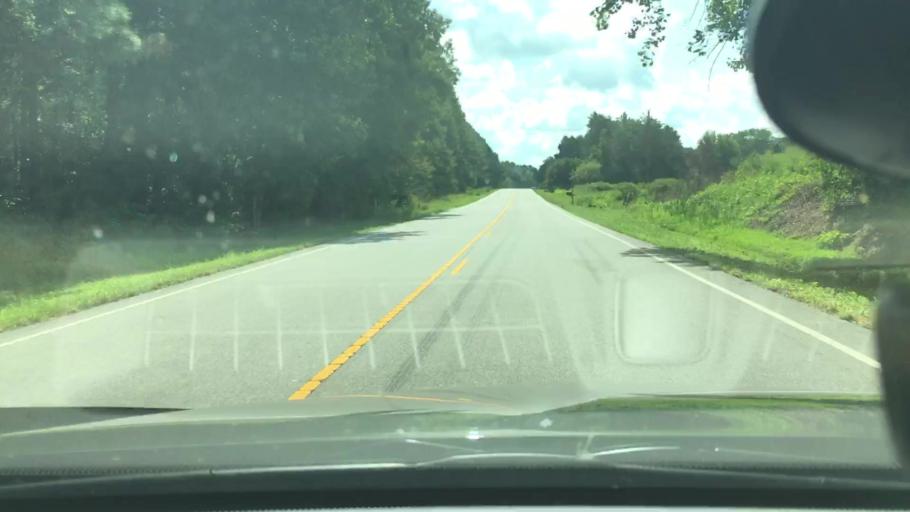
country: US
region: North Carolina
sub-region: Edgecombe County
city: Pinetops
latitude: 35.7397
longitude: -77.5385
